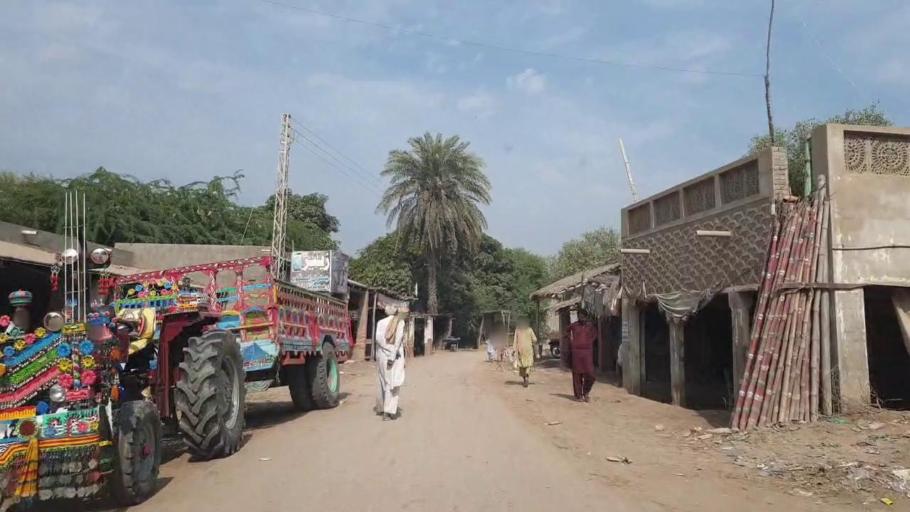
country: PK
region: Sindh
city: Rajo Khanani
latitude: 24.9534
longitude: 68.9777
